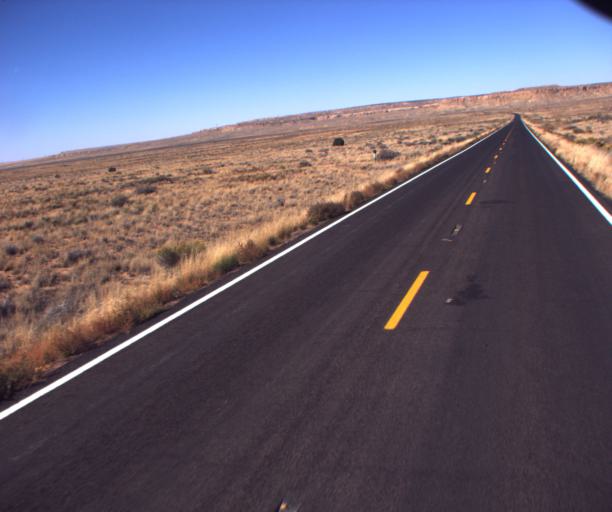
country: US
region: Arizona
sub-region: Navajo County
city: First Mesa
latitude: 35.9659
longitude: -110.6911
